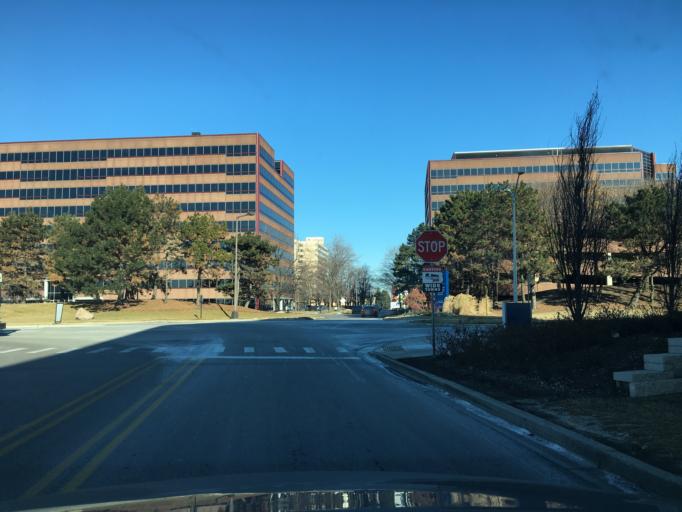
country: US
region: Illinois
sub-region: Cook County
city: Rosemont
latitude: 41.9946
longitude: -87.8827
